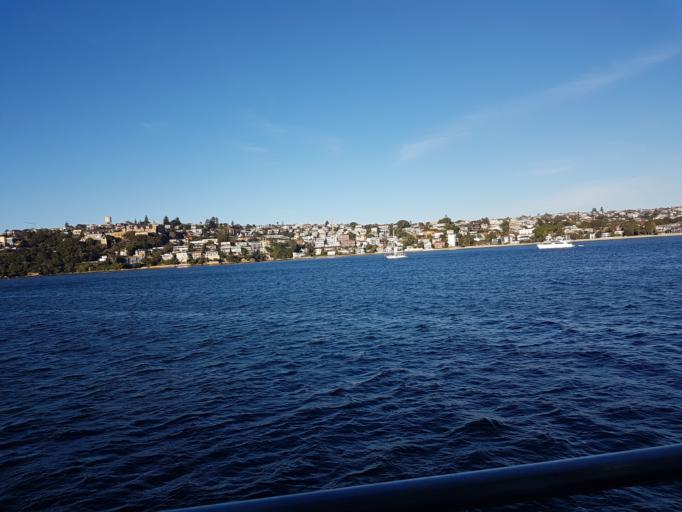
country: AU
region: New South Wales
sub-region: Woollahra
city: Point Piper
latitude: -33.8660
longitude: 151.2612
